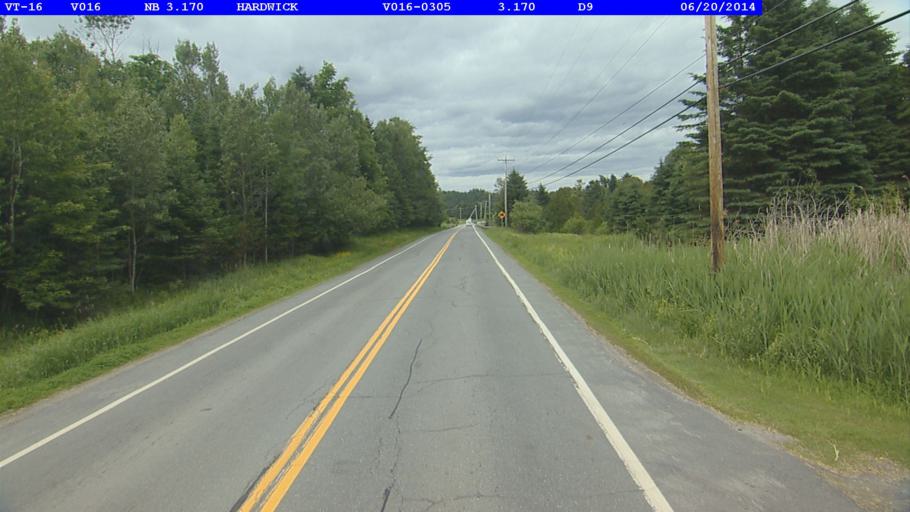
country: US
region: Vermont
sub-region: Caledonia County
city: Hardwick
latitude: 44.5310
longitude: -72.2830
